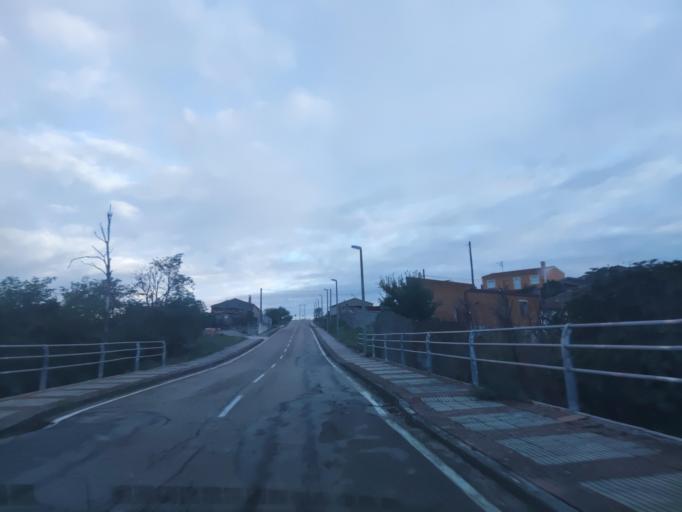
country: ES
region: Castille and Leon
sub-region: Provincia de Salamanca
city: Castillejo de Martin Viejo
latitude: 40.7003
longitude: -6.6473
